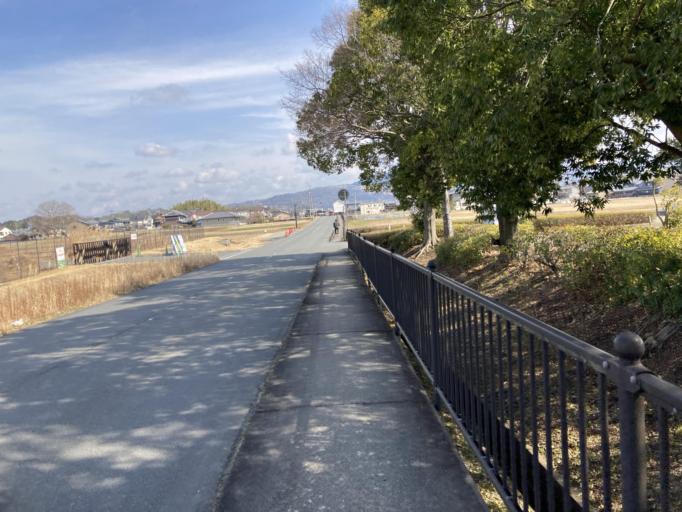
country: JP
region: Nara
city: Nara-shi
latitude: 34.6941
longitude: 135.8000
